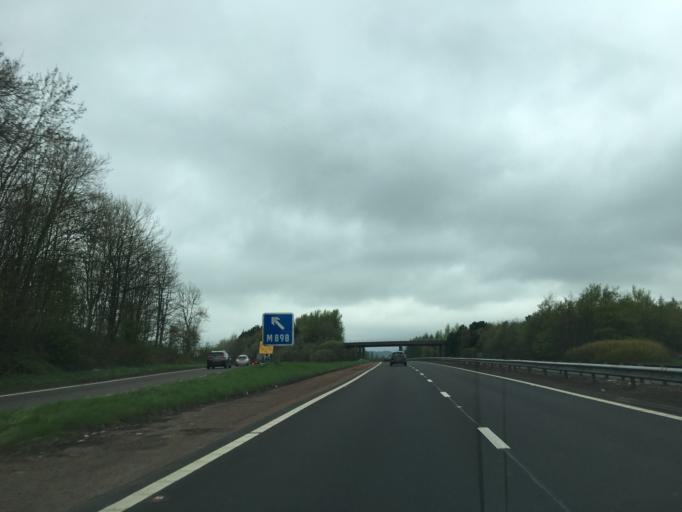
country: GB
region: Scotland
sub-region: Renfrewshire
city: Bishopton
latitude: 55.8982
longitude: -4.4834
